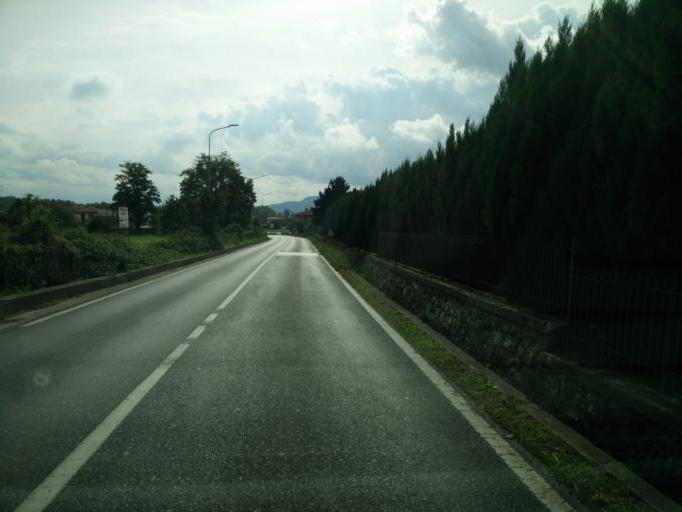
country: IT
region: Tuscany
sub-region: Provincia di Massa-Carrara
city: Filattiera
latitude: 44.3512
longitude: 9.9066
